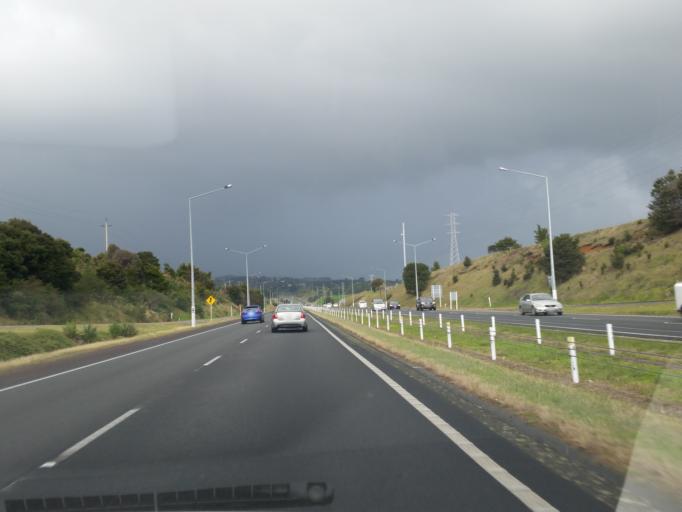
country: NZ
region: Auckland
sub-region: Auckland
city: Pukekohe East
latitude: -37.1445
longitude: 174.9704
